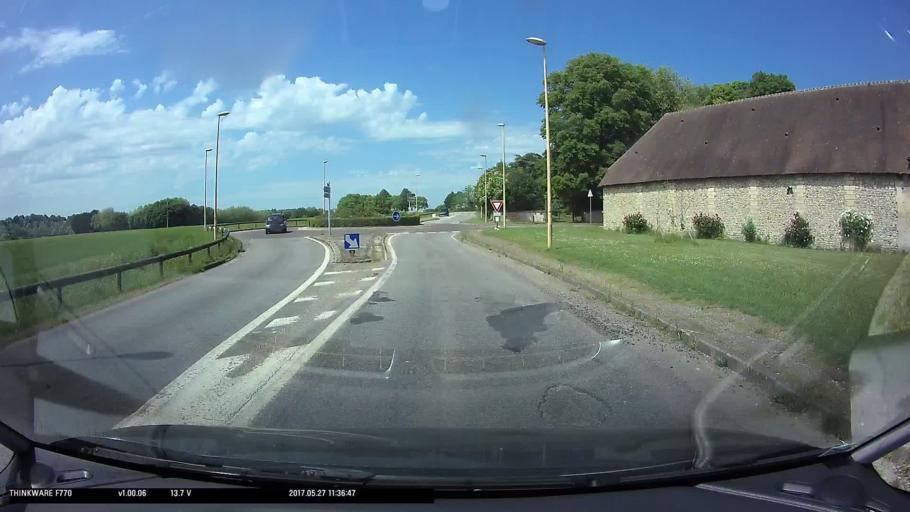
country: FR
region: Haute-Normandie
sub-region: Departement de l'Eure
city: Neaufles-Saint-Martin
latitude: 49.2727
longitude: 1.7338
